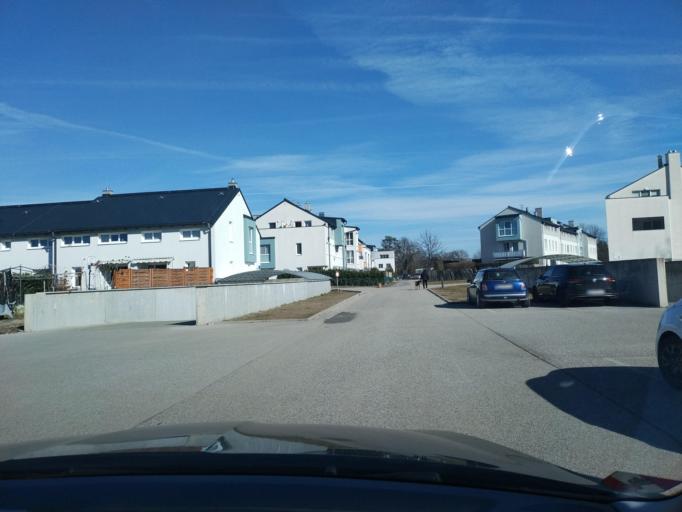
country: AT
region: Lower Austria
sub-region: Politischer Bezirk Neunkirchen
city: Pitten
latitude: 47.7253
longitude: 16.1695
